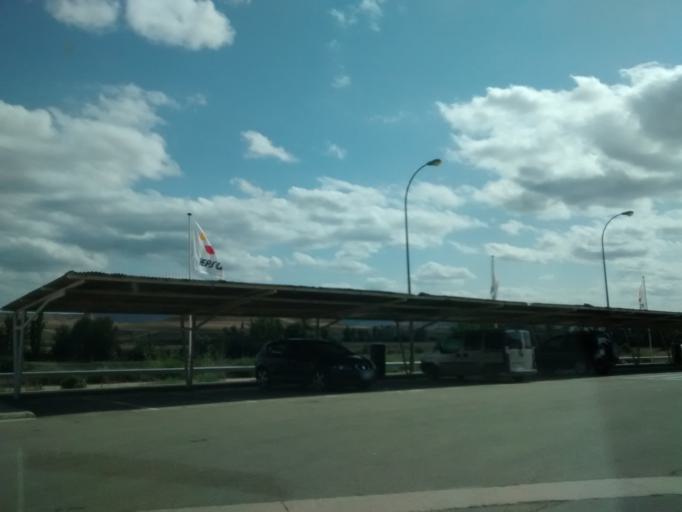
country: ES
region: Castille and Leon
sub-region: Provincia de Soria
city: Santa Maria de Huerta
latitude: 41.2481
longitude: -2.2176
